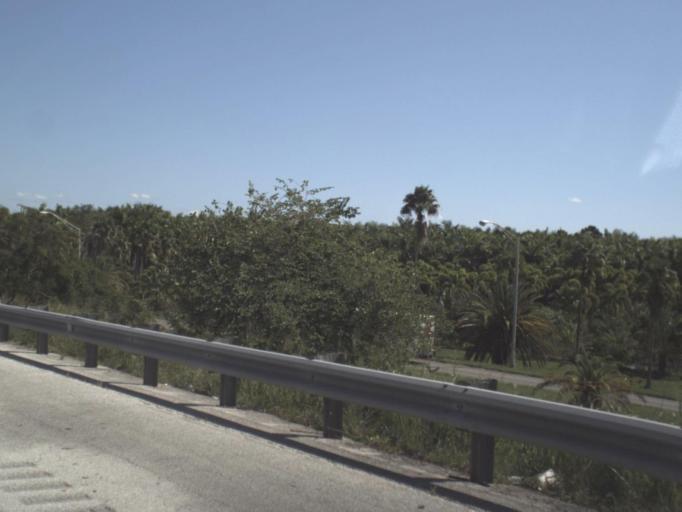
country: US
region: Florida
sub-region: Miami-Dade County
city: Goulds
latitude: 25.5330
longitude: -80.3705
